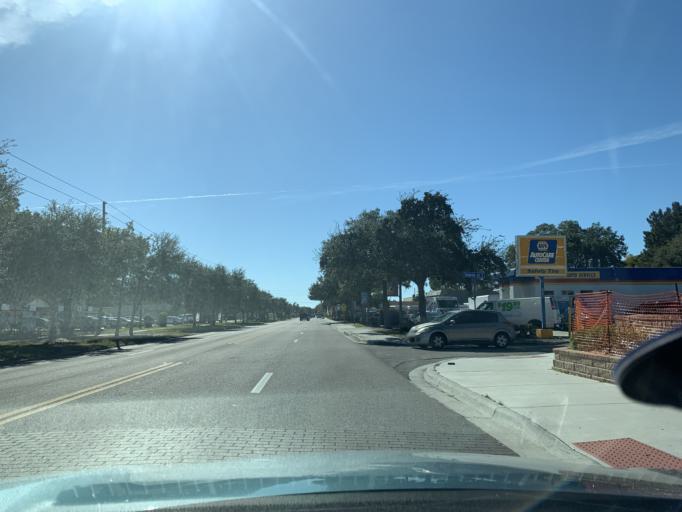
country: US
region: Florida
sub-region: Pinellas County
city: Gulfport
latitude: 27.7519
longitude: -82.6998
